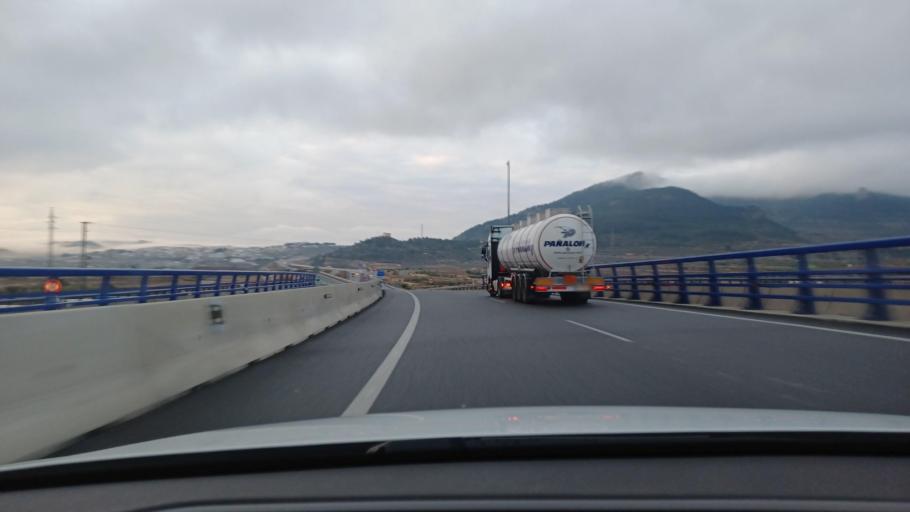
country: ES
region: Valencia
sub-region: Provincia de Valencia
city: La Font de la Figuera
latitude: 38.8274
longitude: -0.8924
